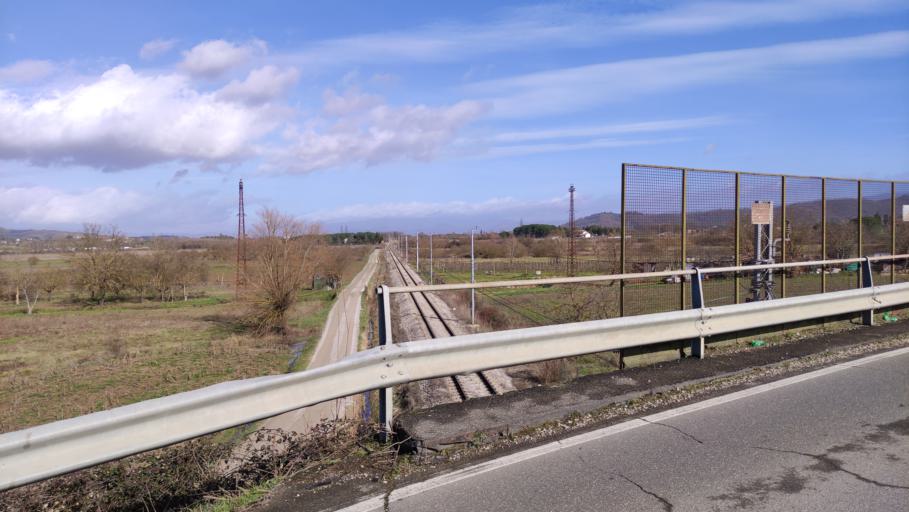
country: IT
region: Tuscany
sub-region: Province of Arezzo
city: Viciomaggio
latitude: 43.4224
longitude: 11.7847
